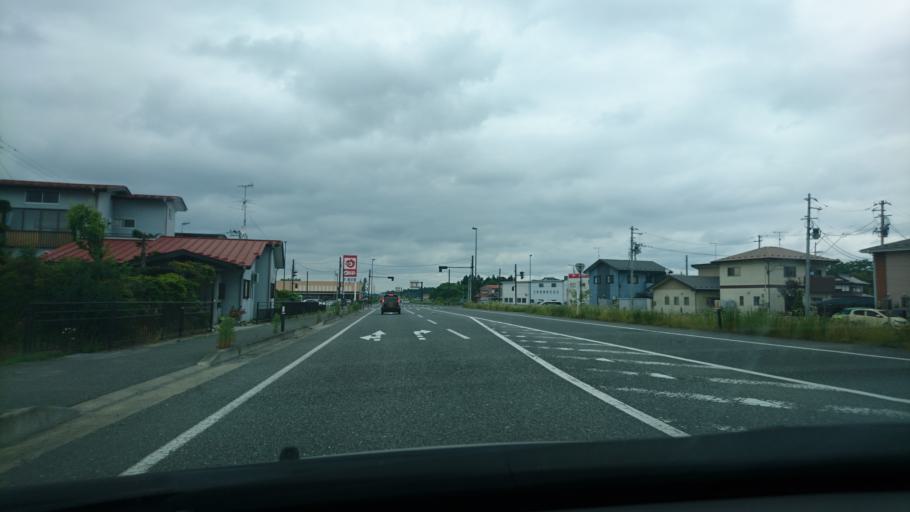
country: JP
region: Miyagi
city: Furukawa
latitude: 38.7327
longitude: 141.0351
